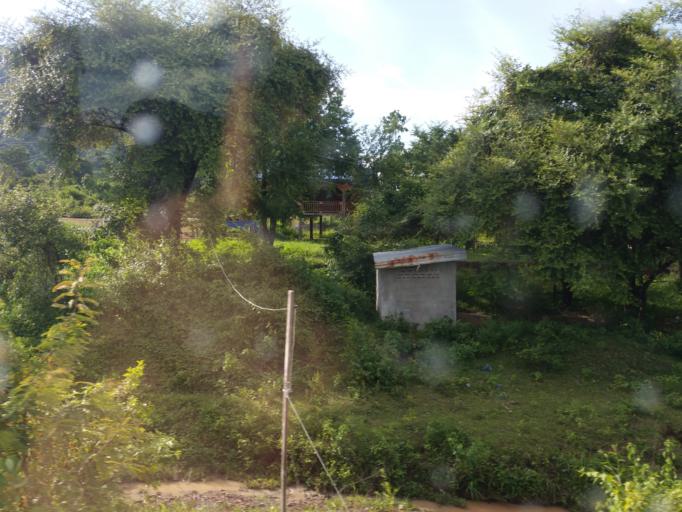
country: TH
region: Changwat Ubon Ratchathani
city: Sirindhorn
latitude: 15.1366
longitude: 105.4975
